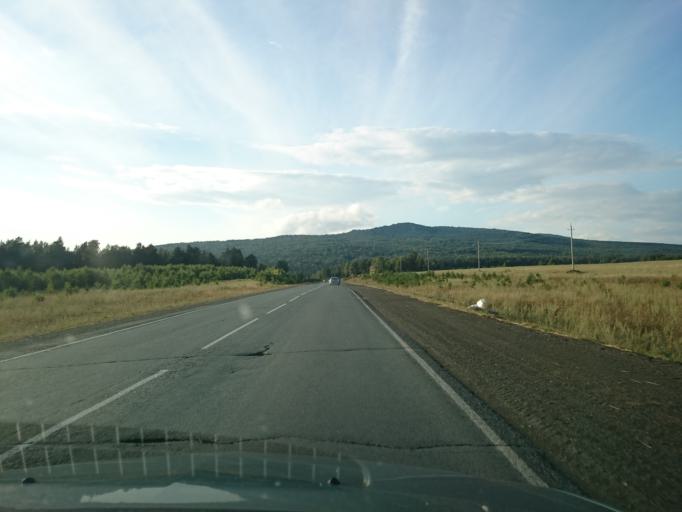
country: RU
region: Bashkortostan
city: Lomovka
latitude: 53.8918
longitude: 58.0945
